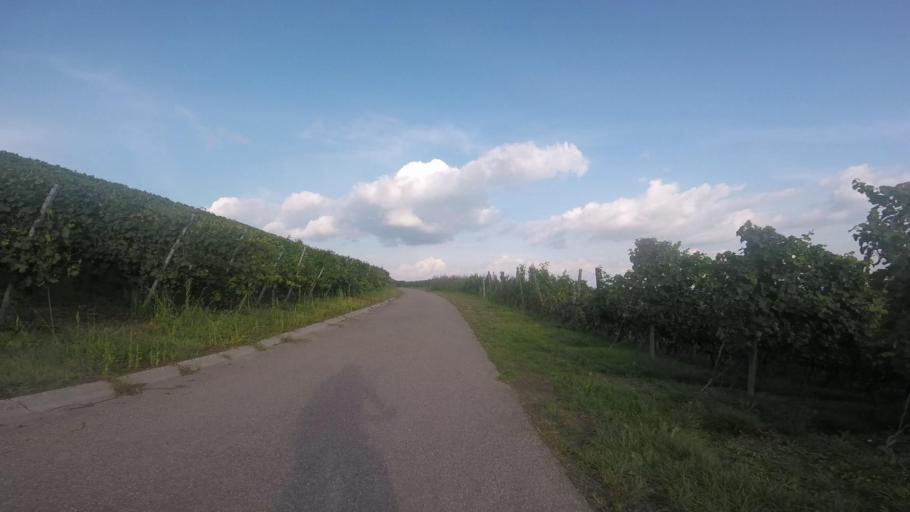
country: DE
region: Baden-Wuerttemberg
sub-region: Regierungsbezirk Stuttgart
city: Aspach
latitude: 48.9973
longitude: 9.3738
